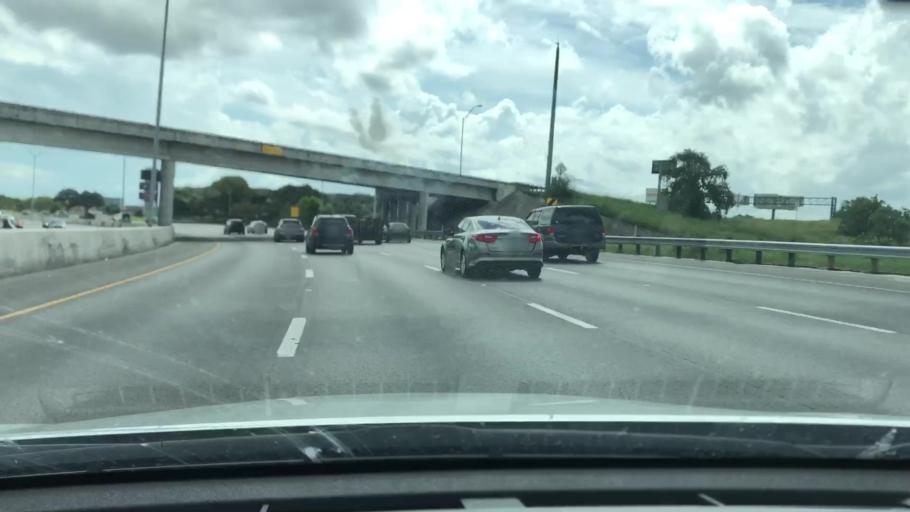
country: US
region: Texas
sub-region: Bexar County
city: Castle Hills
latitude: 29.5380
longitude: -98.4928
